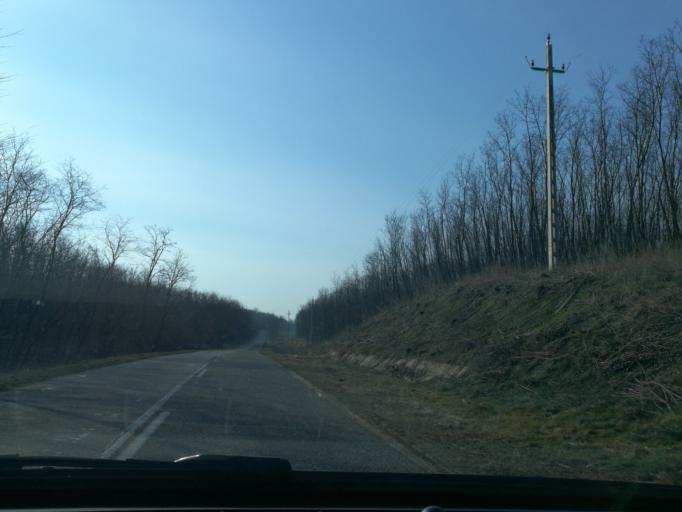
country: HU
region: Szabolcs-Szatmar-Bereg
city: Levelek
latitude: 47.9967
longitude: 21.9665
